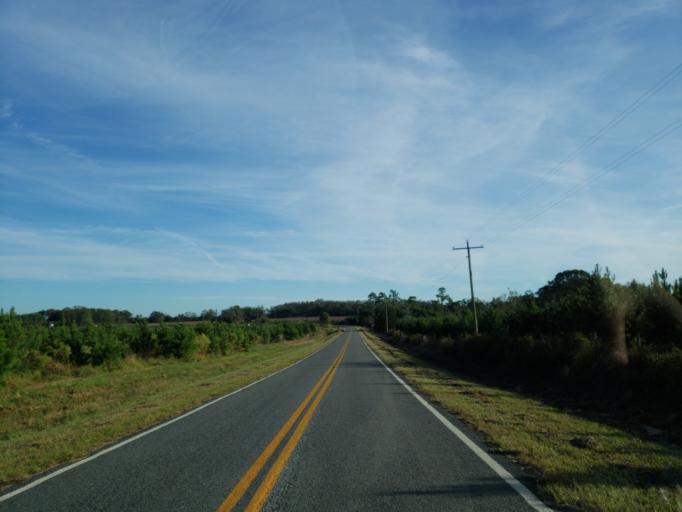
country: US
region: Georgia
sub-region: Dooly County
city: Vienna
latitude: 32.0364
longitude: -83.7527
